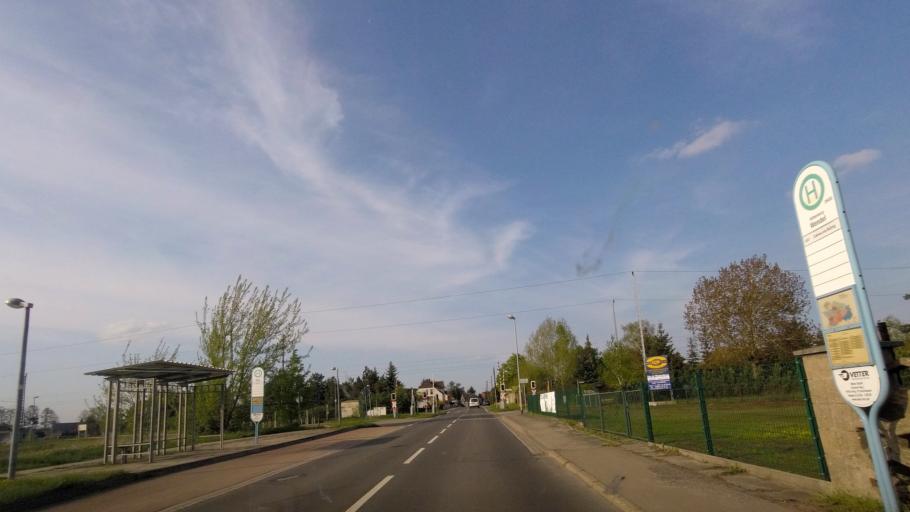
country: DE
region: Saxony-Anhalt
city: Abtsdorf
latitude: 51.8706
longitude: 12.6952
